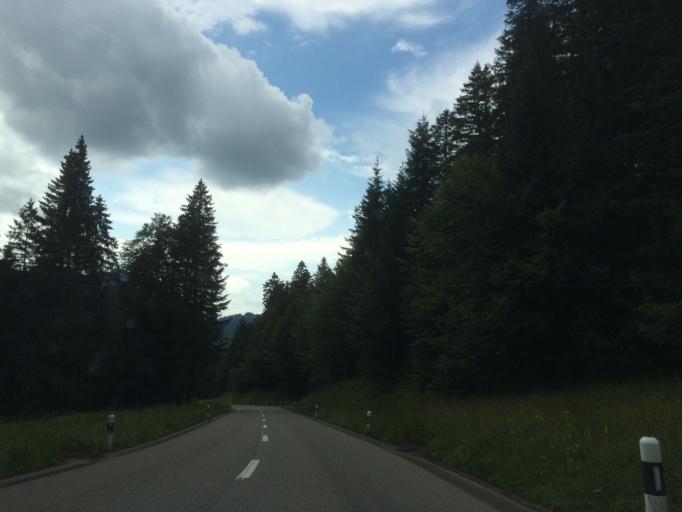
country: CH
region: Appenzell Ausserrhoden
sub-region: Bezirk Hinterland
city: Urnasch
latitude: 47.2533
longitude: 9.2940
